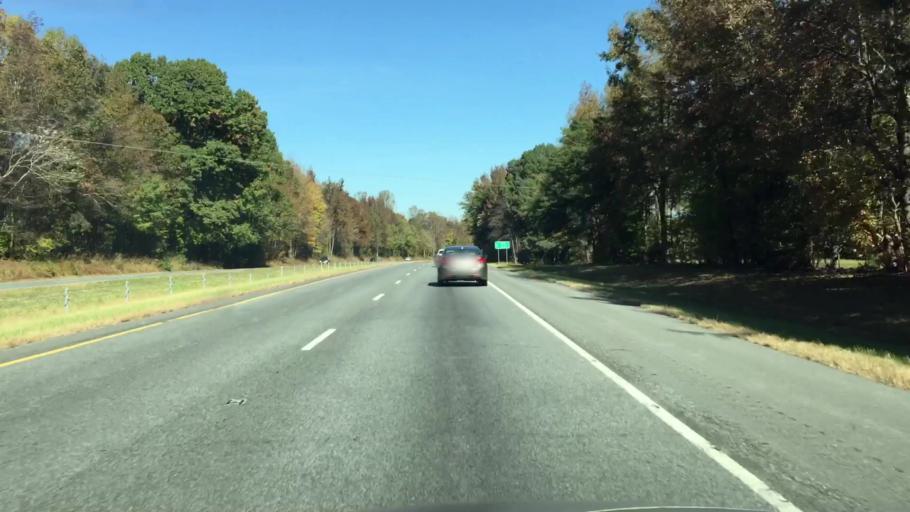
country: US
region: North Carolina
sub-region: Rockingham County
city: Reidsville
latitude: 36.2896
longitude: -79.6412
